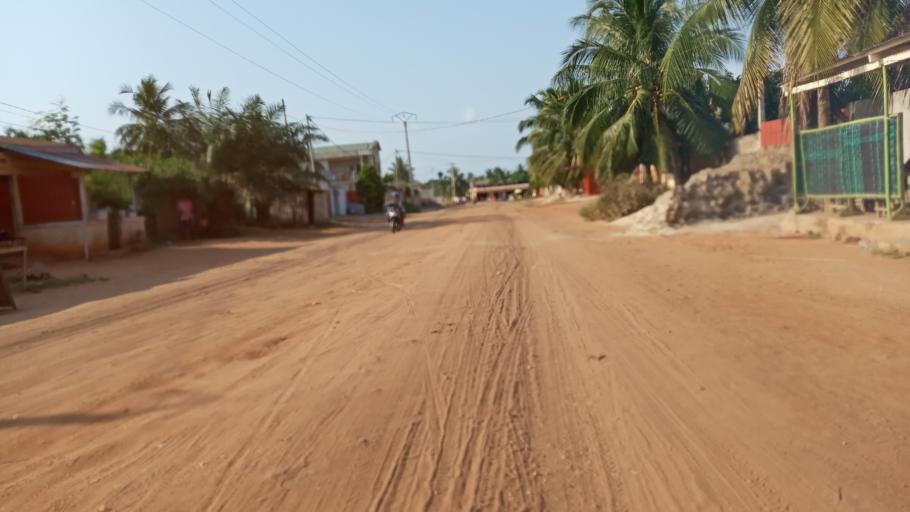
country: TG
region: Maritime
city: Lome
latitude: 6.1778
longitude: 1.1511
